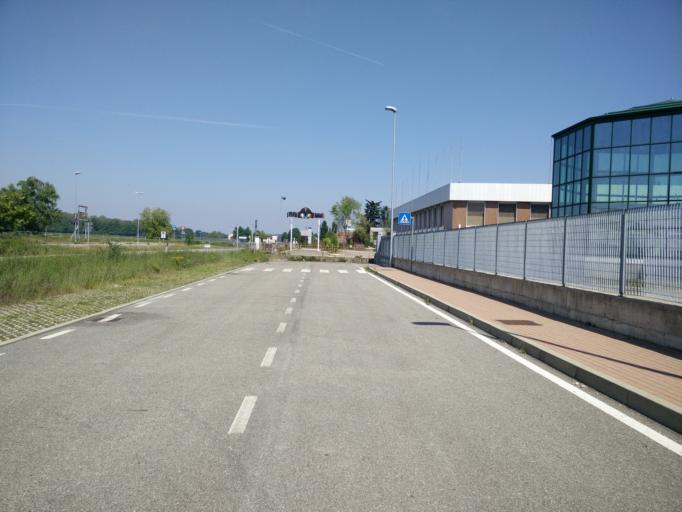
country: IT
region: Piedmont
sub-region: Provincia di Torino
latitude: 44.9545
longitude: 7.5575
